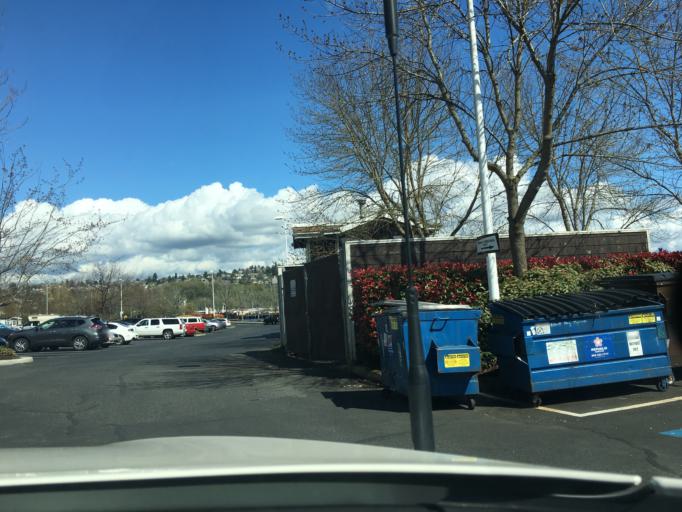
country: US
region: Washington
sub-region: King County
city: Seattle
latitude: 47.6307
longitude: -122.3904
